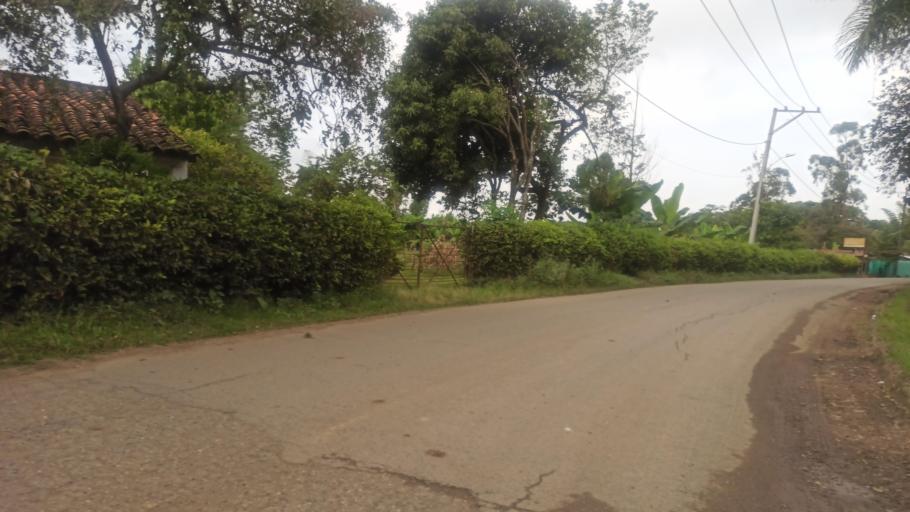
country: CO
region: Valle del Cauca
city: Jamundi
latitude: 3.1999
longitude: -76.5077
